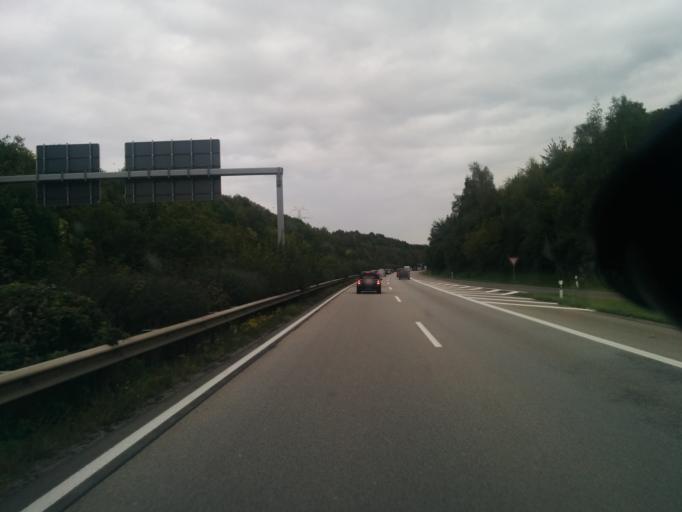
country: DE
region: Rheinland-Pfalz
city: Bad Neuenahr-Ahrweiler
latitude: 50.5755
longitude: 7.1197
